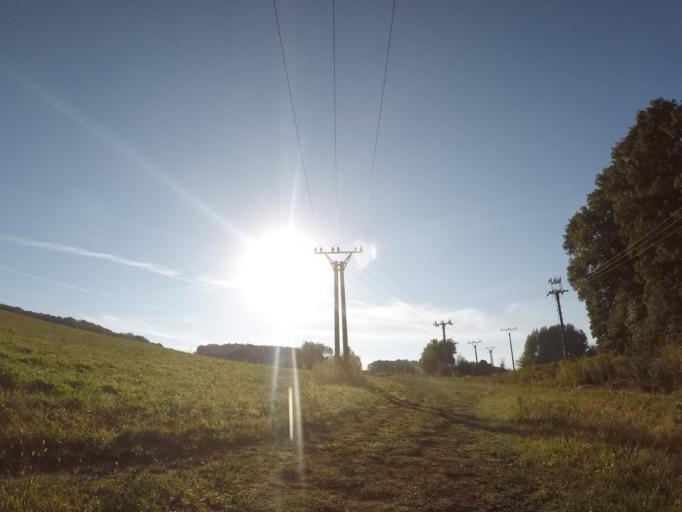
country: SK
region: Kosicky
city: Kosice
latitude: 48.7326
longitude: 21.1865
